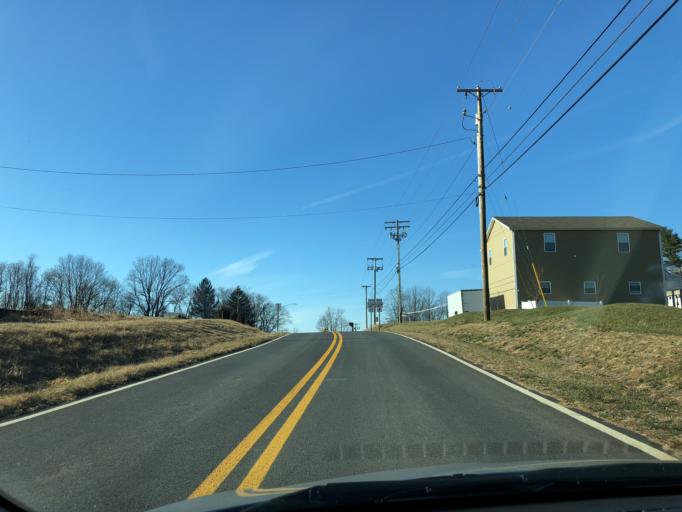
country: US
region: Maryland
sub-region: Baltimore County
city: Kingsville
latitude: 39.4600
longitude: -76.4545
